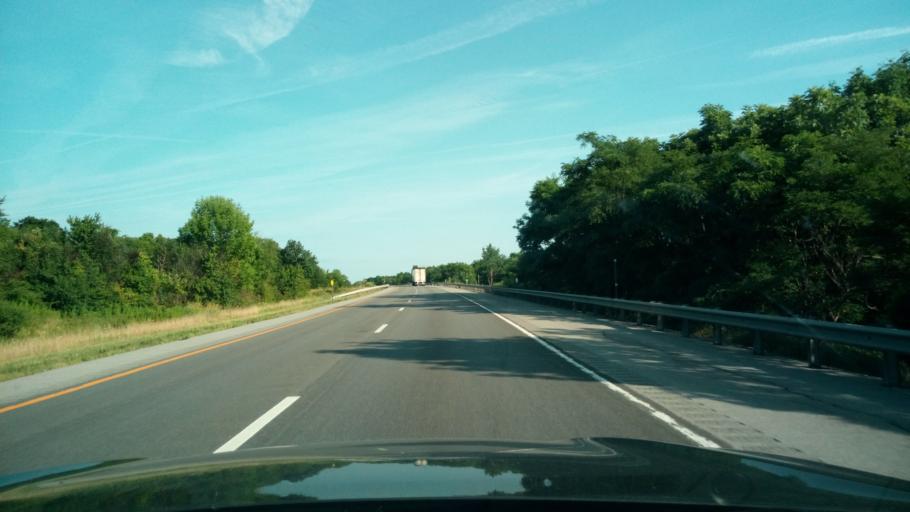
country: US
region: New York
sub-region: Livingston County
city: Mount Morris
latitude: 42.6406
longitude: -77.7878
